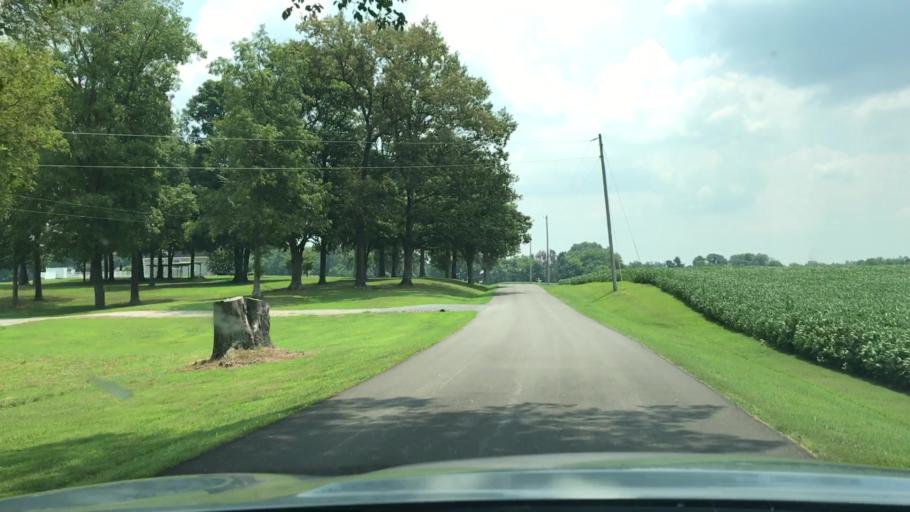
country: US
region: Kentucky
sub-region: Todd County
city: Elkton
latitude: 36.7678
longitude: -87.1402
